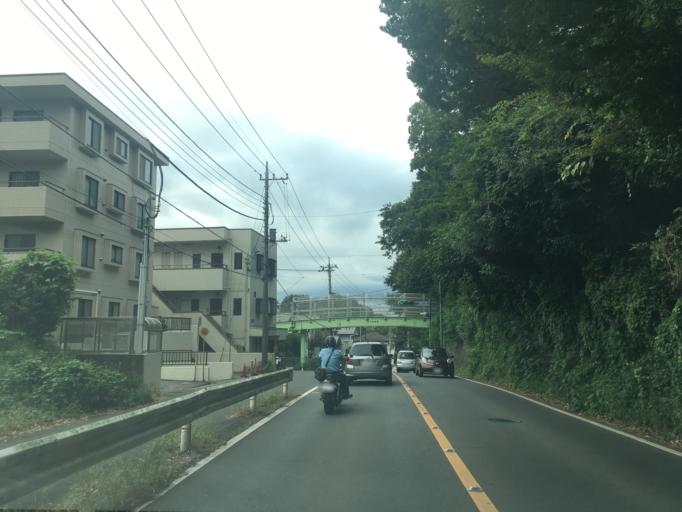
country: JP
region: Saitama
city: Tokorozawa
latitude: 35.7813
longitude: 139.4263
